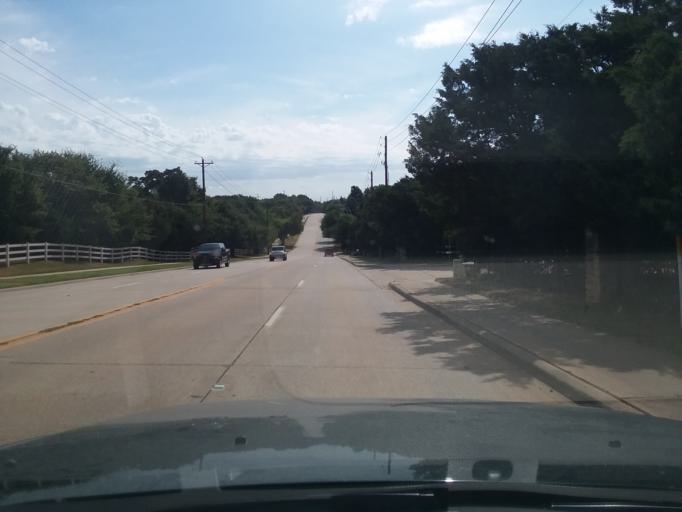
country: US
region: Texas
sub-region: Denton County
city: Flower Mound
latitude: 33.0138
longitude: -97.0837
